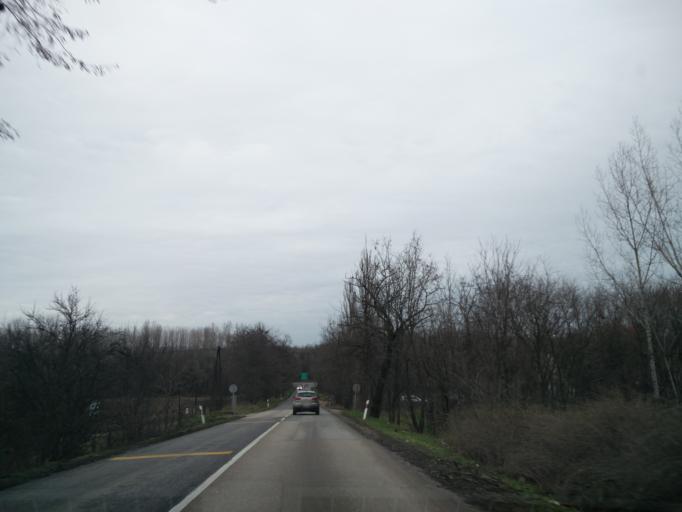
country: HU
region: Pest
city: Gyomro
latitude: 47.4274
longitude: 19.4200
